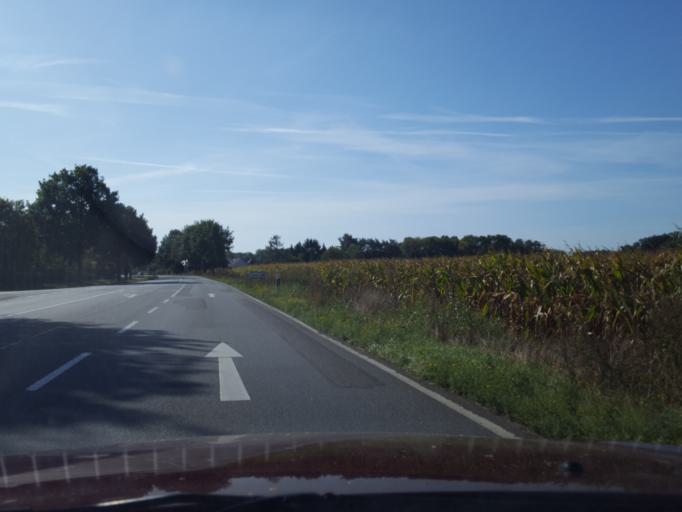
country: DE
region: Lower Saxony
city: Eystrup
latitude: 52.7871
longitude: 9.2114
